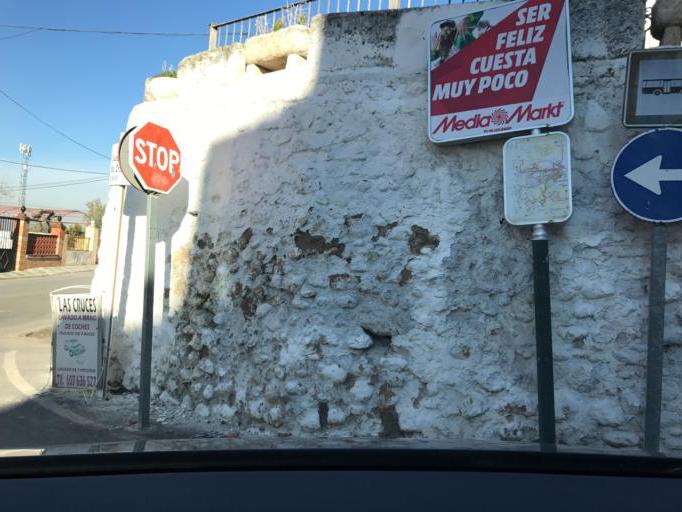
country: ES
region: Andalusia
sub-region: Provincia de Granada
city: Pulianas
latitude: 37.2221
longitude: -3.6097
